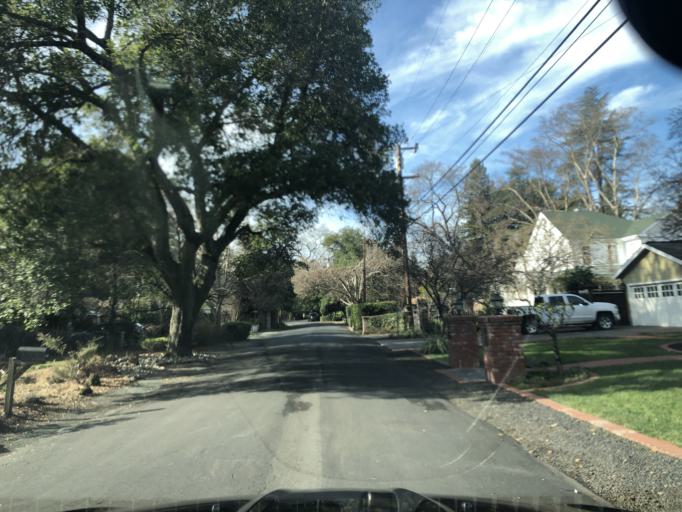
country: US
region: California
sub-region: Contra Costa County
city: Saranap
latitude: 37.8850
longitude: -122.0806
